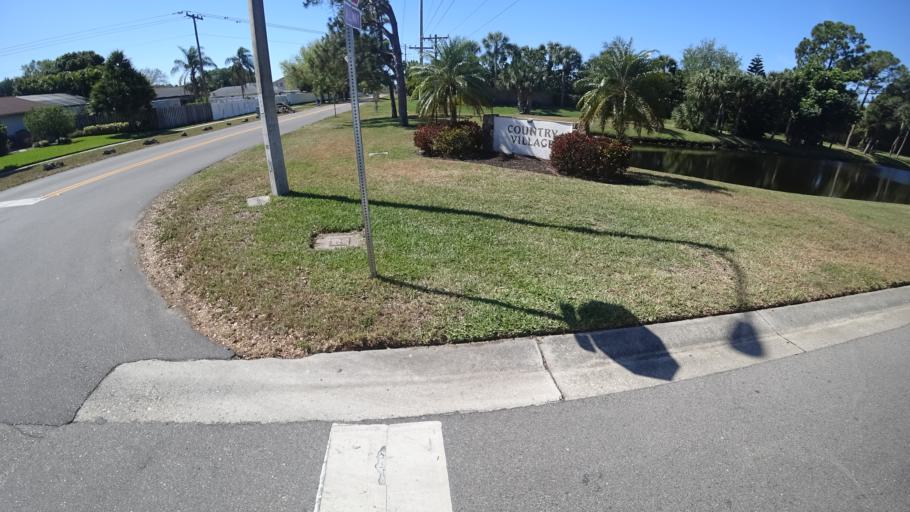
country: US
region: Florida
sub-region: Manatee County
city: West Bradenton
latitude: 27.4742
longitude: -82.6328
